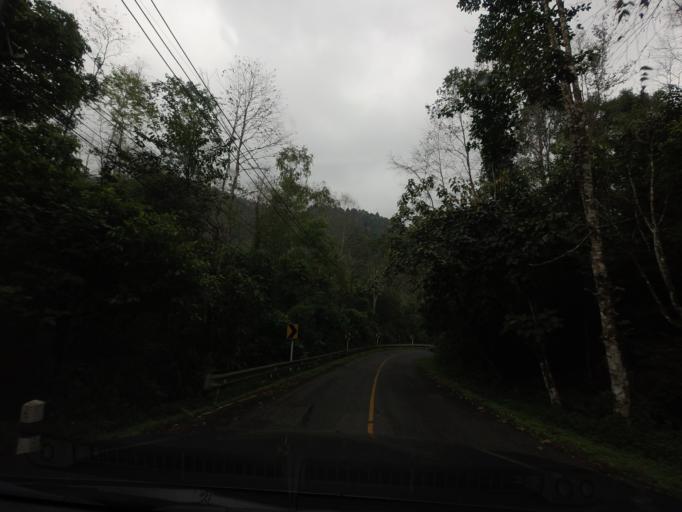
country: TH
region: Nan
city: Bo Kluea
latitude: 19.1978
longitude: 101.0817
